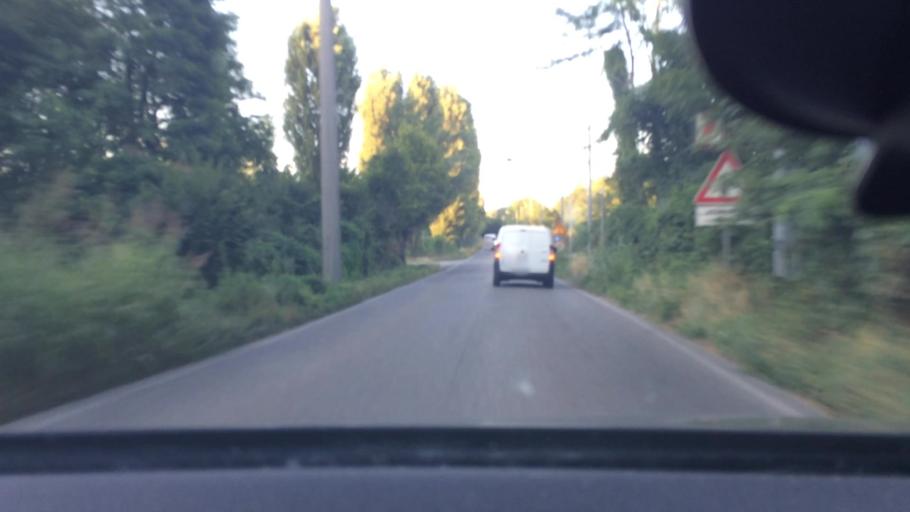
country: IT
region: Lombardy
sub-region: Citta metropolitana di Milano
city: Rescaldina
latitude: 45.6293
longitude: 8.9671
